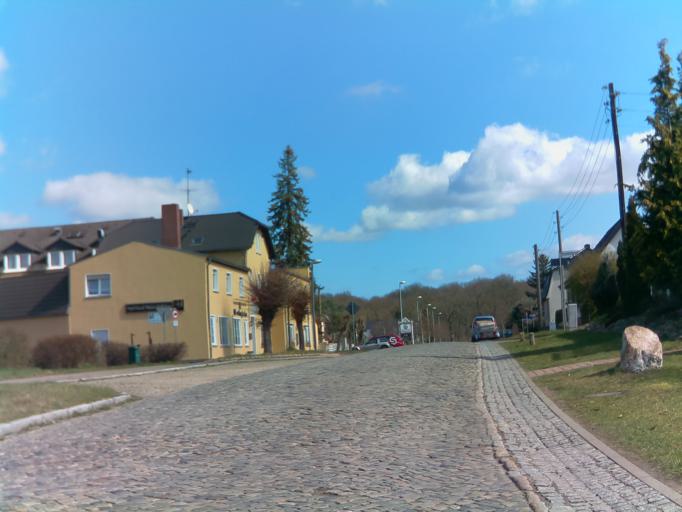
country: DE
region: Saxony-Anhalt
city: Klieken
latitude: 51.8889
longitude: 12.3732
